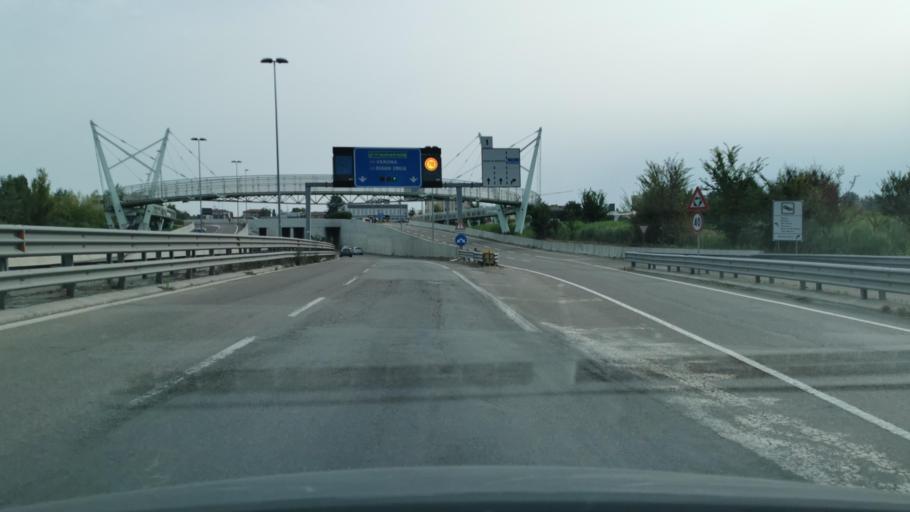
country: IT
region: Emilia-Romagna
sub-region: Provincia di Modena
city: Modena
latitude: 44.6314
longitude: 10.9557
